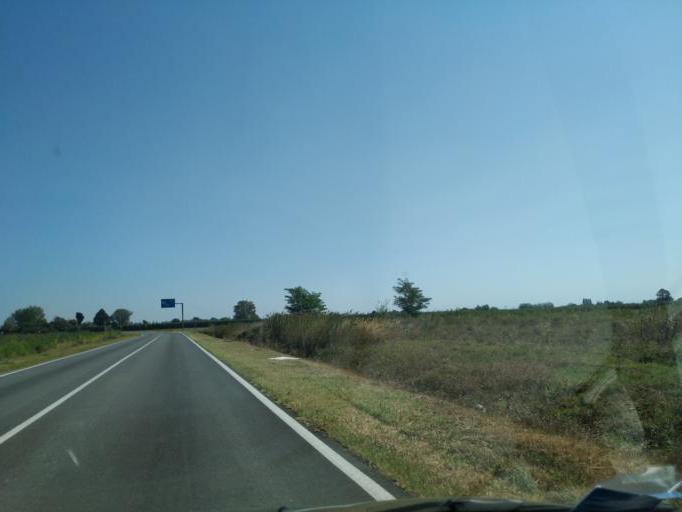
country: IT
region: Emilia-Romagna
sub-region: Provincia di Ferrara
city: Copparo
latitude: 44.8884
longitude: 11.8401
